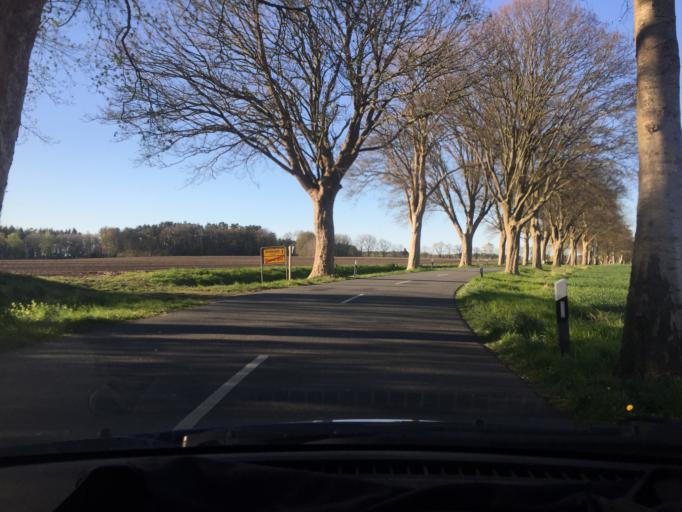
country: DE
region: Lower Saxony
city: Weste
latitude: 53.0644
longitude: 10.7247
